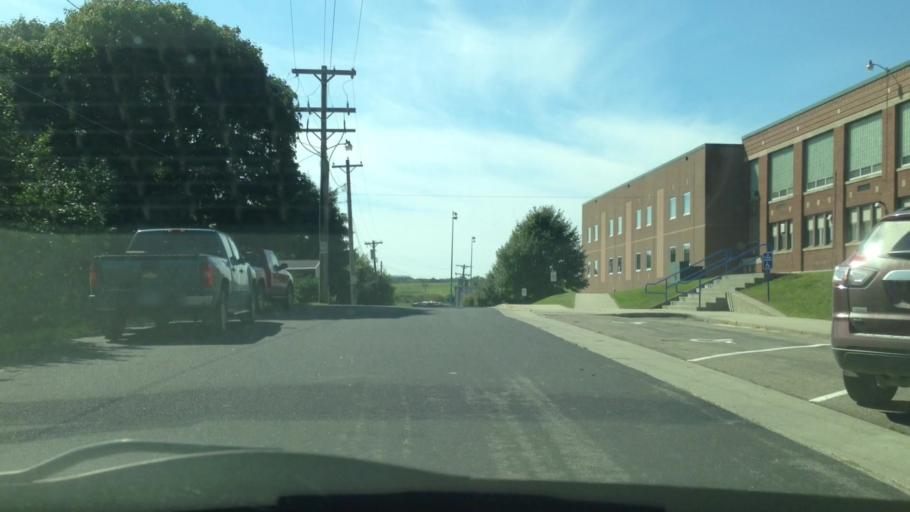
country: US
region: Minnesota
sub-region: Houston County
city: Spring Grove
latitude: 43.5203
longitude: -91.7729
